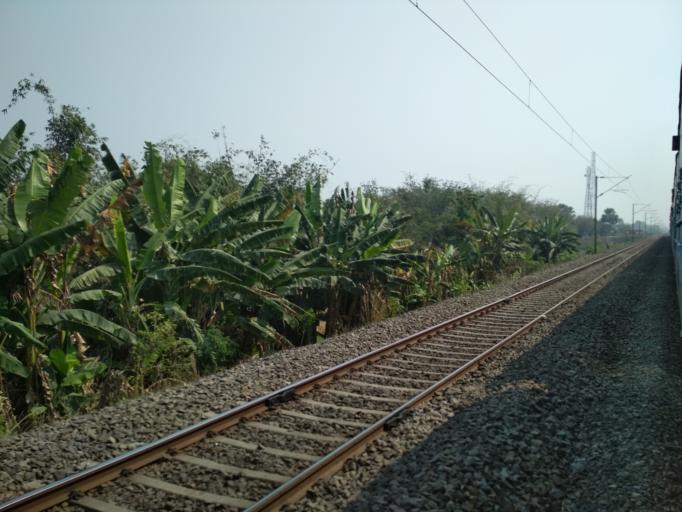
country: IN
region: Bihar
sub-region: Khagaria
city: Khagaria
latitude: 25.5083
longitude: 86.5246
